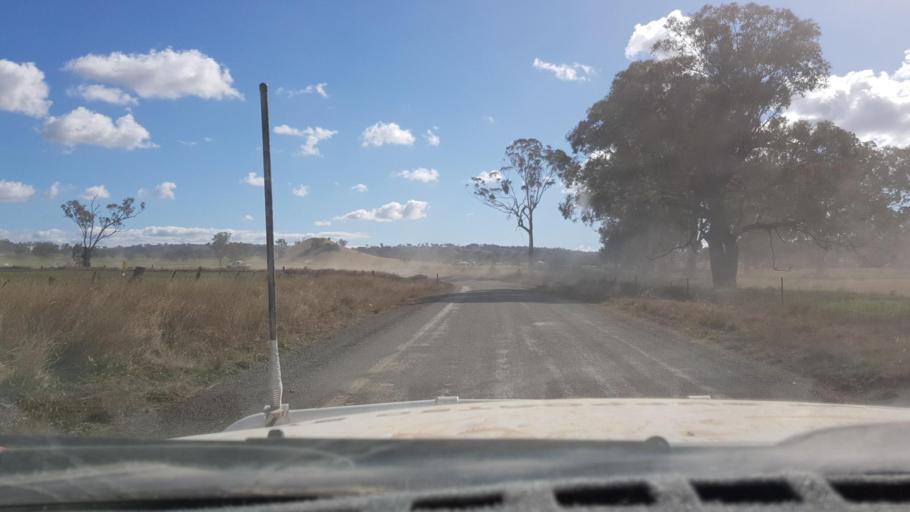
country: AU
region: New South Wales
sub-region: Tamworth Municipality
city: Manilla
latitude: -30.5873
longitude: 150.4890
